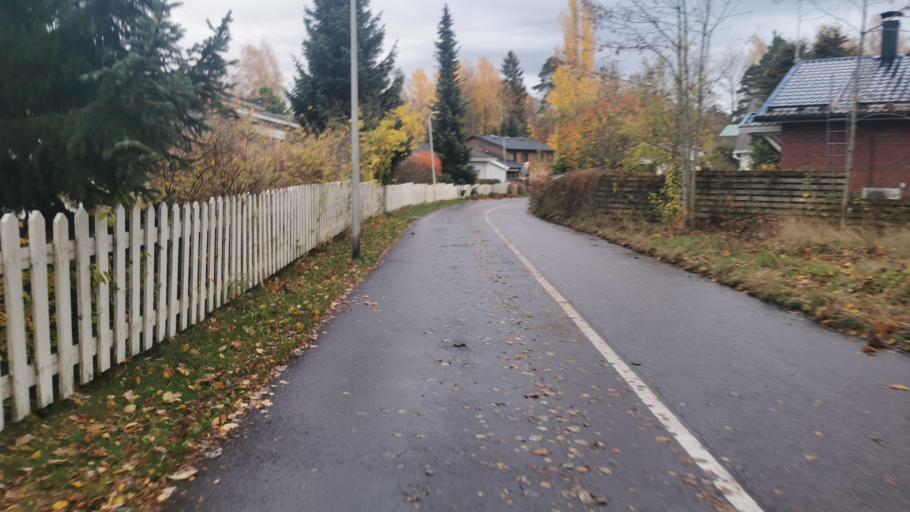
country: FI
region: Uusimaa
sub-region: Helsinki
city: Kerava
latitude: 60.4077
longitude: 25.0880
